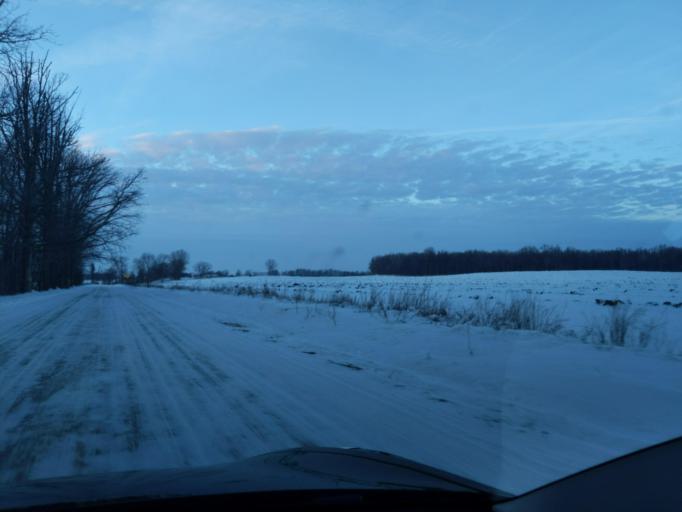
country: US
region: Michigan
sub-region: Ingham County
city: Williamston
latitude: 42.5655
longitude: -84.3099
